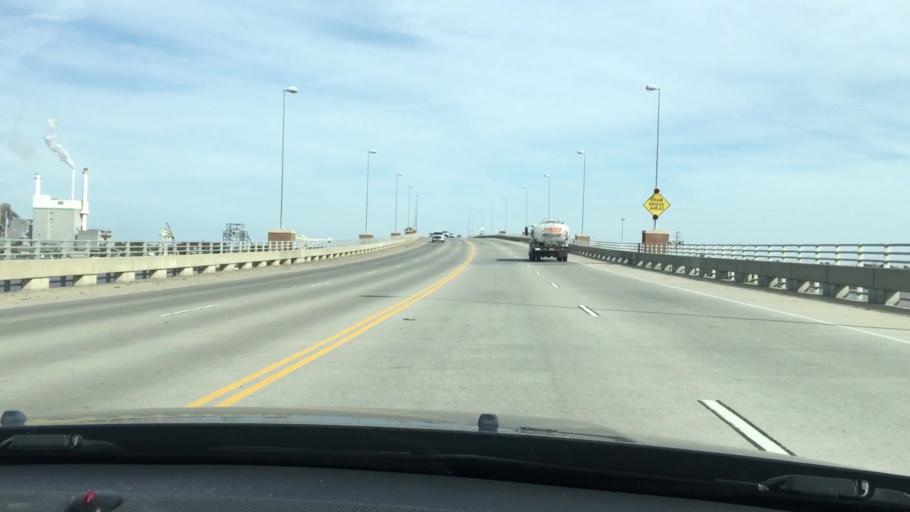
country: US
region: Virginia
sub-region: King William County
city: West Point
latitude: 37.5317
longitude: -76.8108
